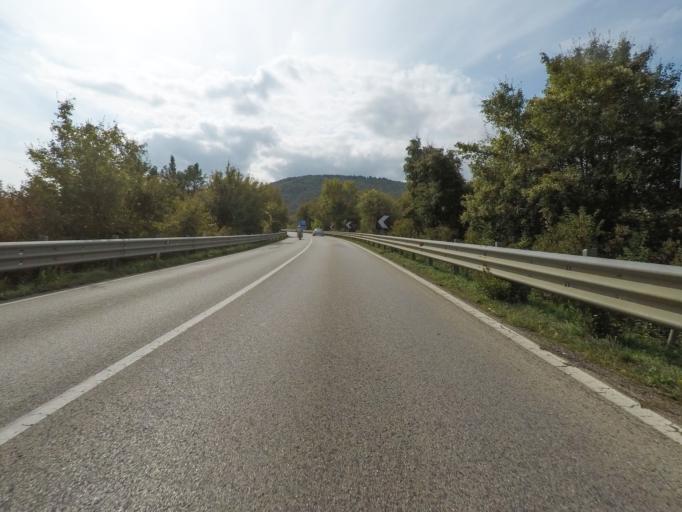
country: IT
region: Tuscany
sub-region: Provincia di Siena
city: Murlo
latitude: 43.1489
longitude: 11.2864
